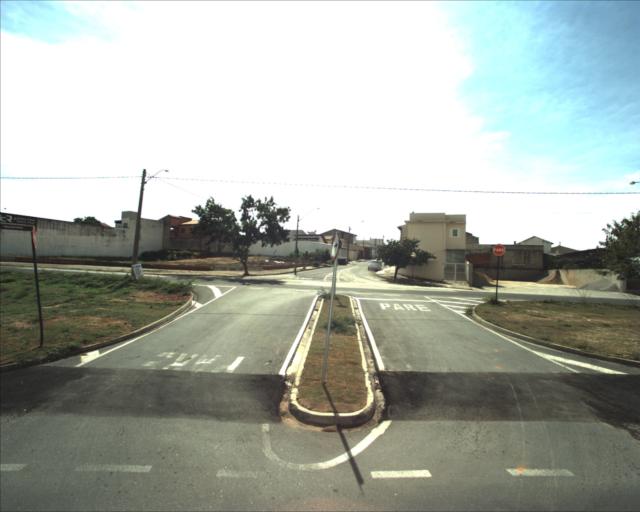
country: BR
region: Sao Paulo
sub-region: Sorocaba
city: Sorocaba
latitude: -23.5156
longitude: -47.5182
